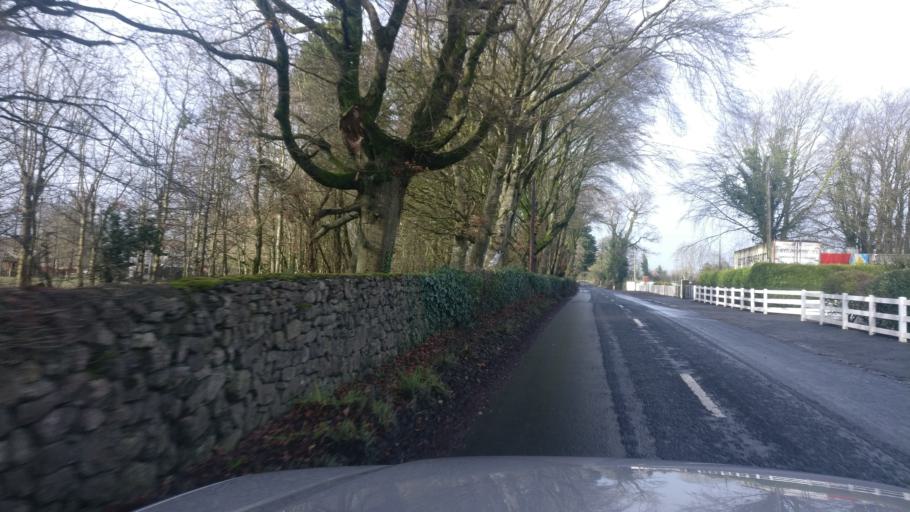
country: IE
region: Connaught
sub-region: County Galway
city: Loughrea
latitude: 53.2850
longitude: -8.5923
